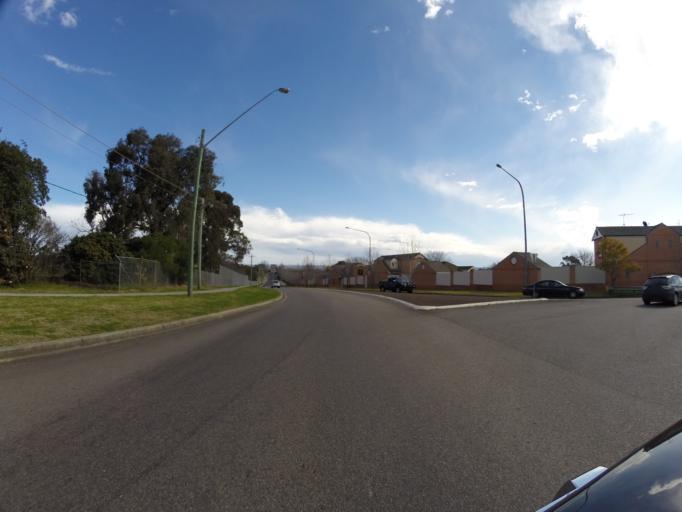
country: AU
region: New South Wales
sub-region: Camden
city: Narellan
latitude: -34.0434
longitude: 150.7265
